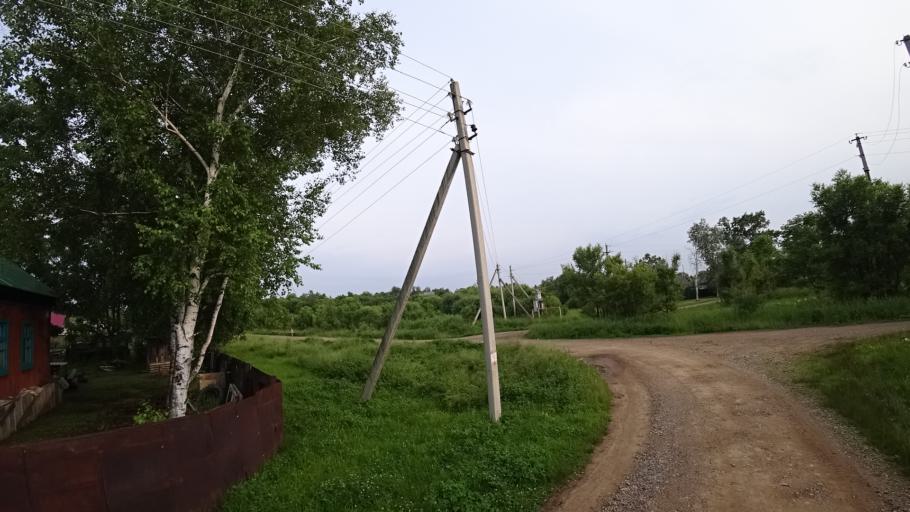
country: RU
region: Primorskiy
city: Novosysoyevka
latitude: 44.2443
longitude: 133.3605
